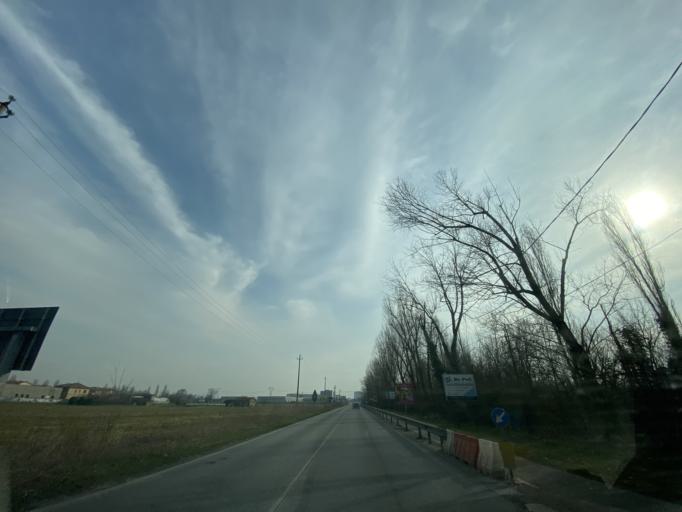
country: IT
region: Lombardy
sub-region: Citta metropolitana di Milano
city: Carugate
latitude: 45.5452
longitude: 9.3346
